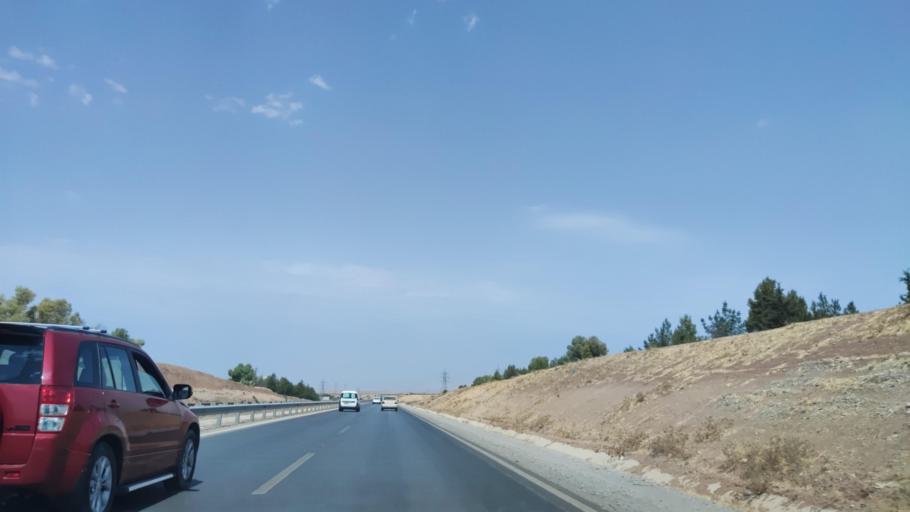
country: IQ
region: Arbil
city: Shaqlawah
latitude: 36.5007
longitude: 44.3586
